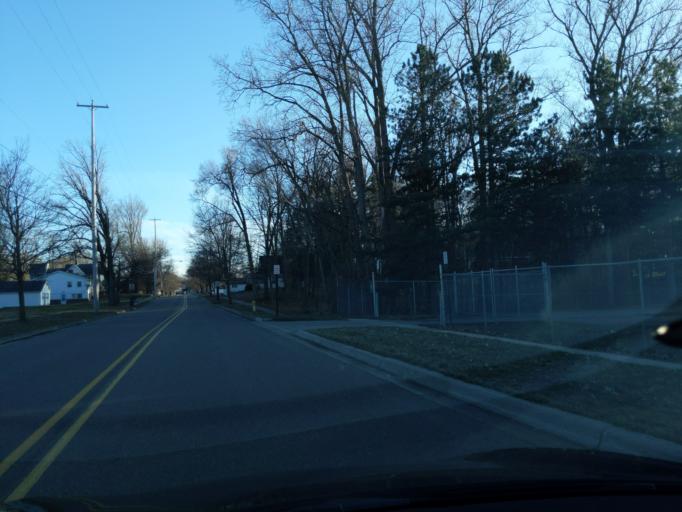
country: US
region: Michigan
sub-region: Ingham County
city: Mason
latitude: 42.5867
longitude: -84.4431
